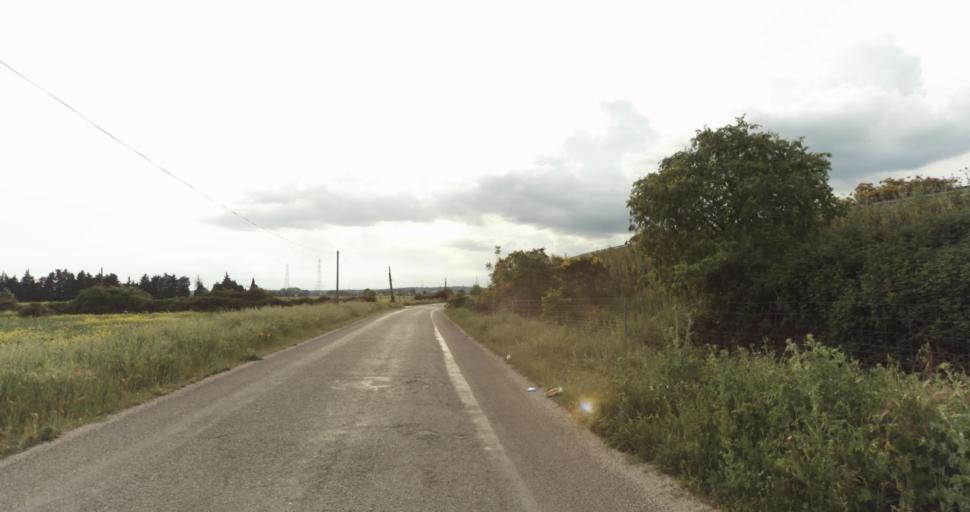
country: FR
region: Languedoc-Roussillon
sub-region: Departement du Gard
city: Nimes
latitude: 43.8072
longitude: 4.3513
